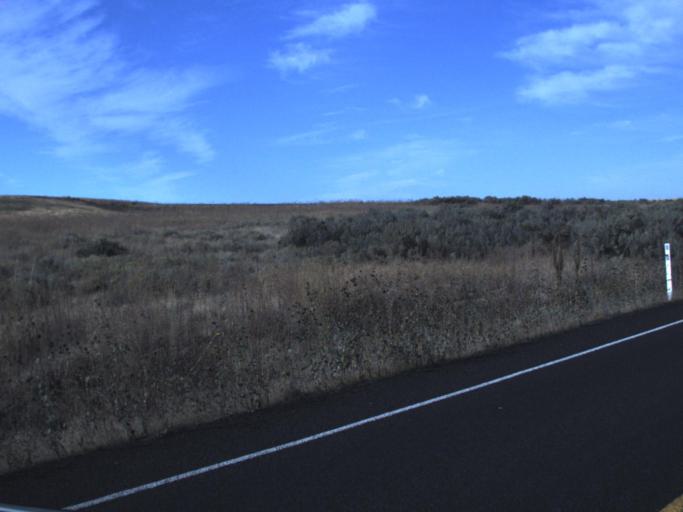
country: US
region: Washington
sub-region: Franklin County
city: Connell
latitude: 46.6296
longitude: -118.7293
